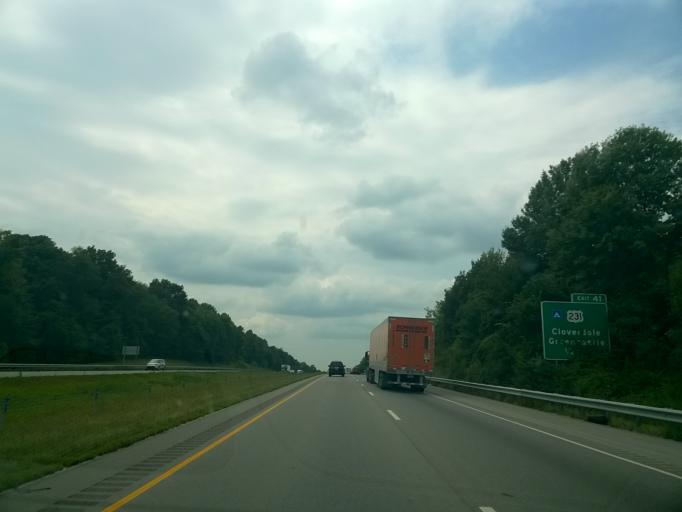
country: US
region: Indiana
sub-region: Putnam County
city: Cloverdale
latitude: 39.5338
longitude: -86.7878
